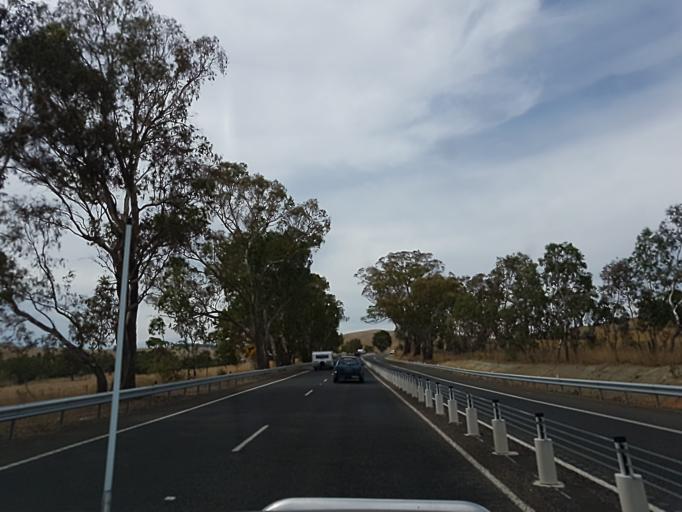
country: AU
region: Victoria
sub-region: Murrindindi
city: Alexandra
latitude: -37.1985
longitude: 145.4726
